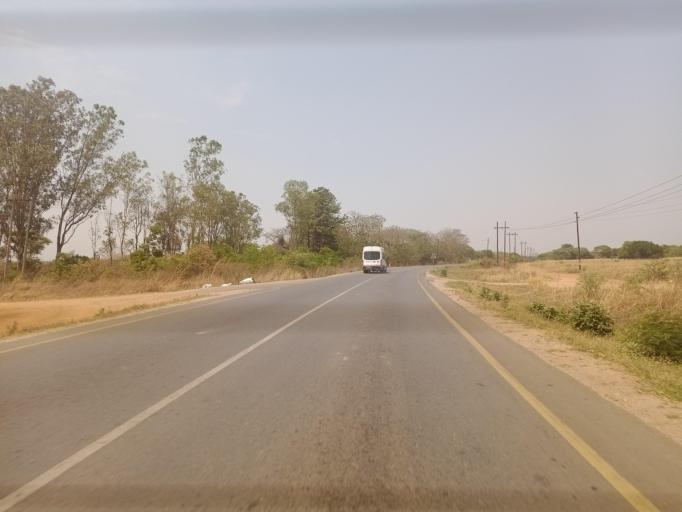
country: ZM
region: Lusaka
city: Lusaka
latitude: -15.2772
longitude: 28.4029
